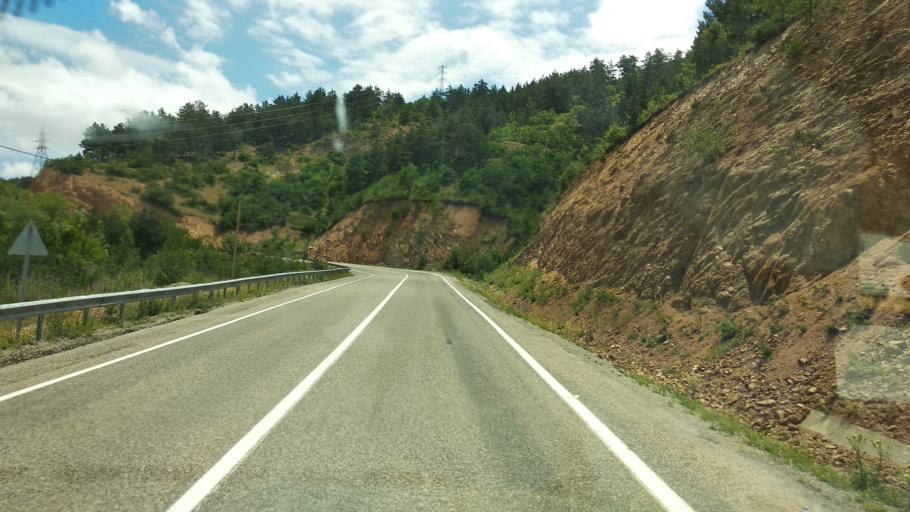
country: TR
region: Gumushane
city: Kose
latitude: 40.2987
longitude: 39.5659
